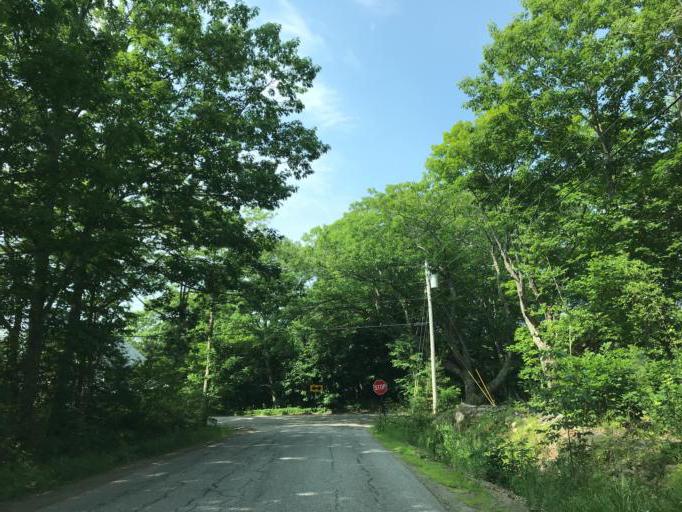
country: US
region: Maine
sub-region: Knox County
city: Hope
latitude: 44.2221
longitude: -69.1744
